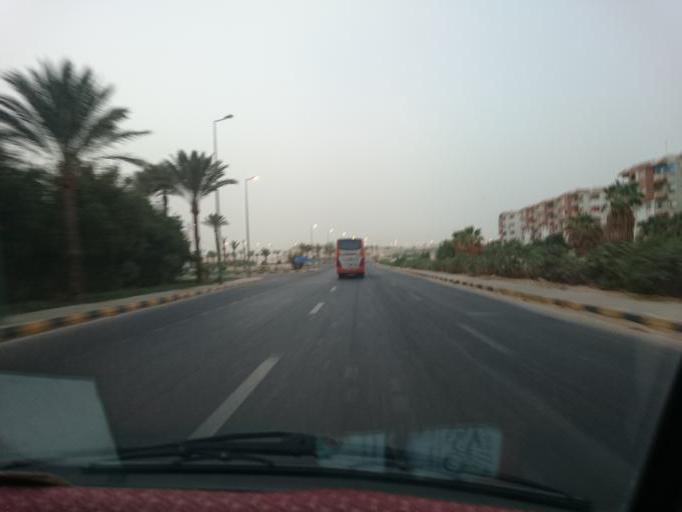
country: EG
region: Red Sea
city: Hurghada
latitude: 27.2115
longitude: 33.8188
